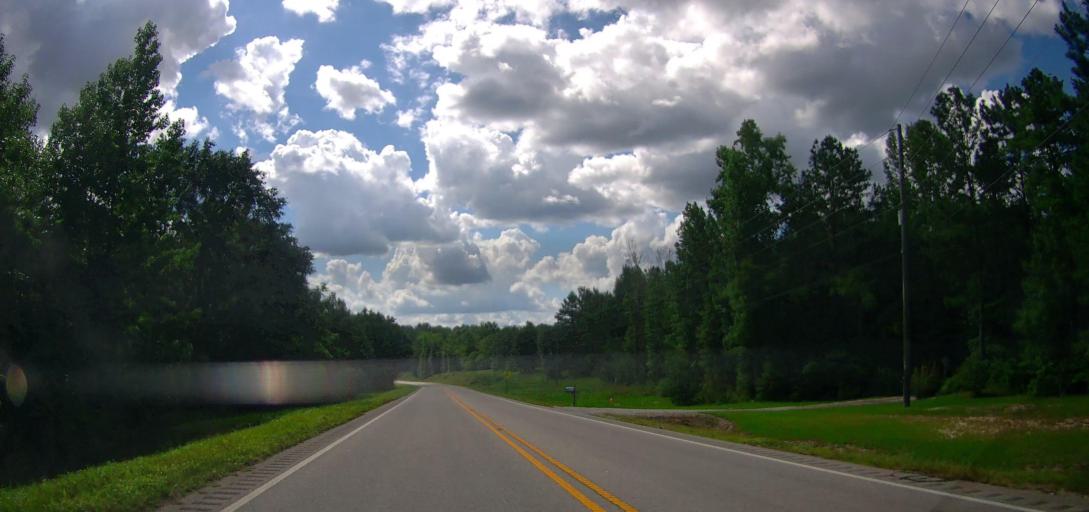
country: US
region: Alabama
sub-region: Lee County
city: Auburn
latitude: 32.4458
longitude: -85.5067
